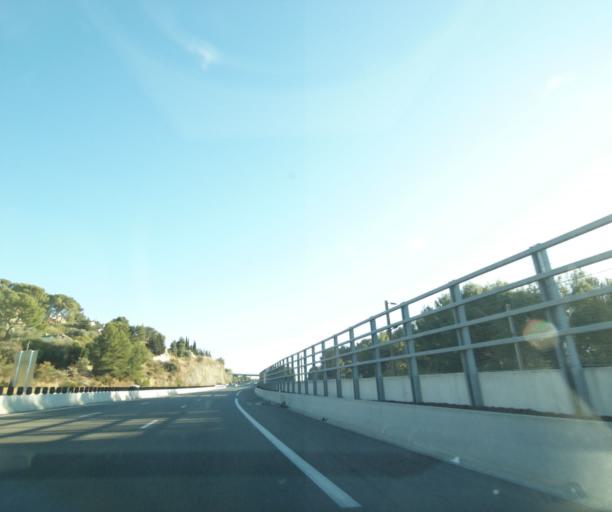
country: FR
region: Provence-Alpes-Cote d'Azur
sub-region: Departement des Bouches-du-Rhone
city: Ceyreste
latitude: 43.2064
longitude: 5.6313
